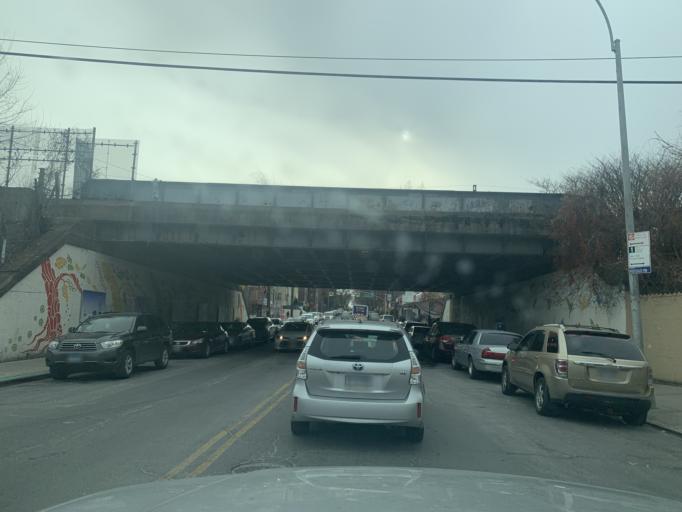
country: US
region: New York
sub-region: Queens County
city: Borough of Queens
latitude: 40.7270
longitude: -73.8644
